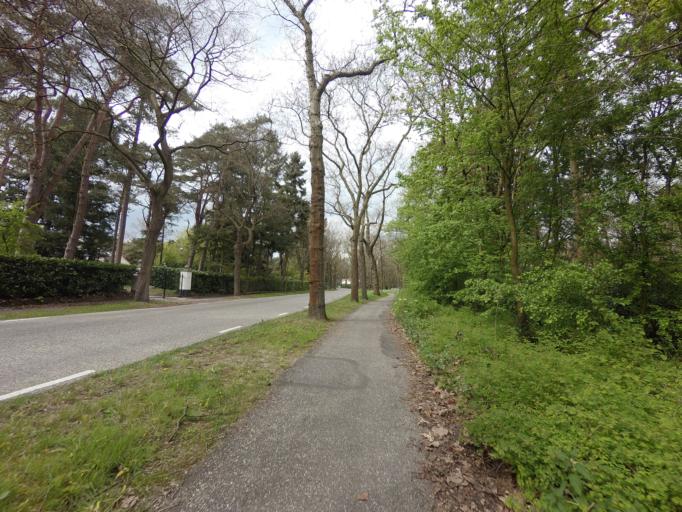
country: NL
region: Utrecht
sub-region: Gemeente Zeist
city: Zeist
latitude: 52.1288
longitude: 5.2325
